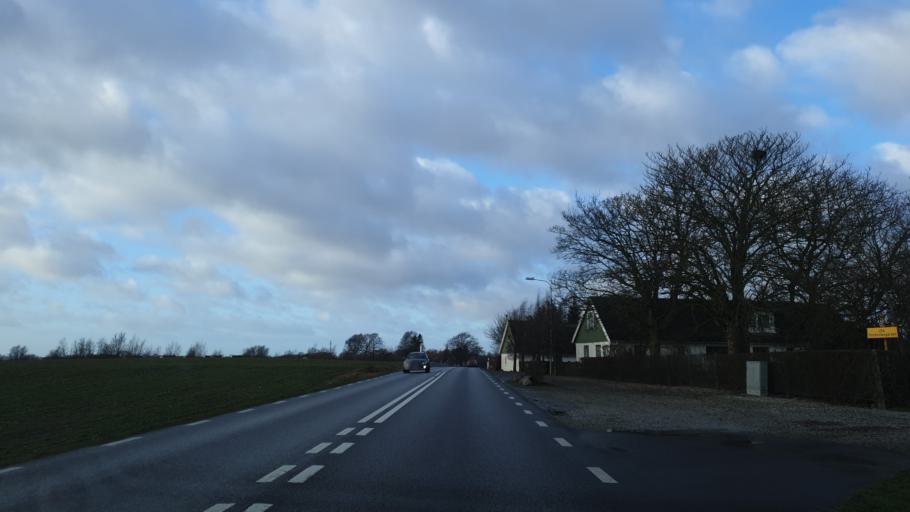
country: SE
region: Skane
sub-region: Trelleborgs Kommun
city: Trelleborg
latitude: 55.4617
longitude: 13.1504
